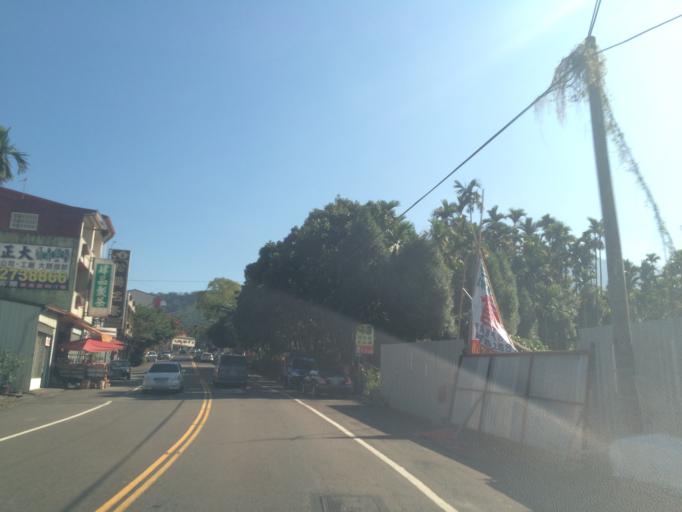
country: TW
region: Taiwan
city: Lugu
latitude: 23.7347
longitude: 120.7632
